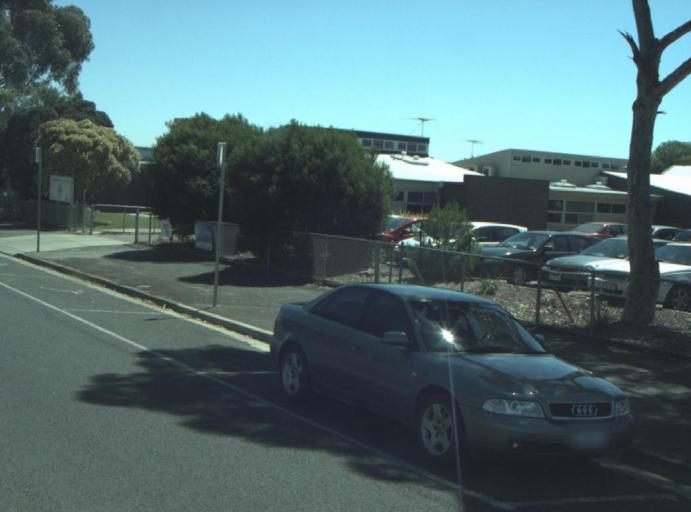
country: AU
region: Victoria
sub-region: Greater Geelong
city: Breakwater
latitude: -38.1981
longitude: 144.3474
